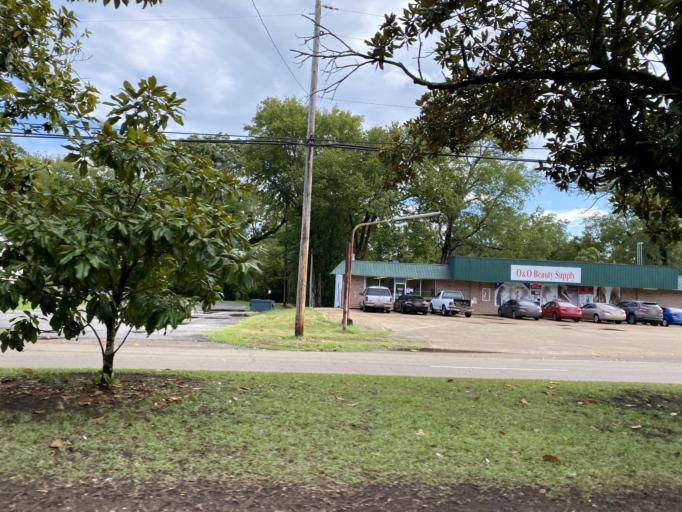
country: US
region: Mississippi
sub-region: Monroe County
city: Aberdeen
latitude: 33.8255
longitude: -88.5501
